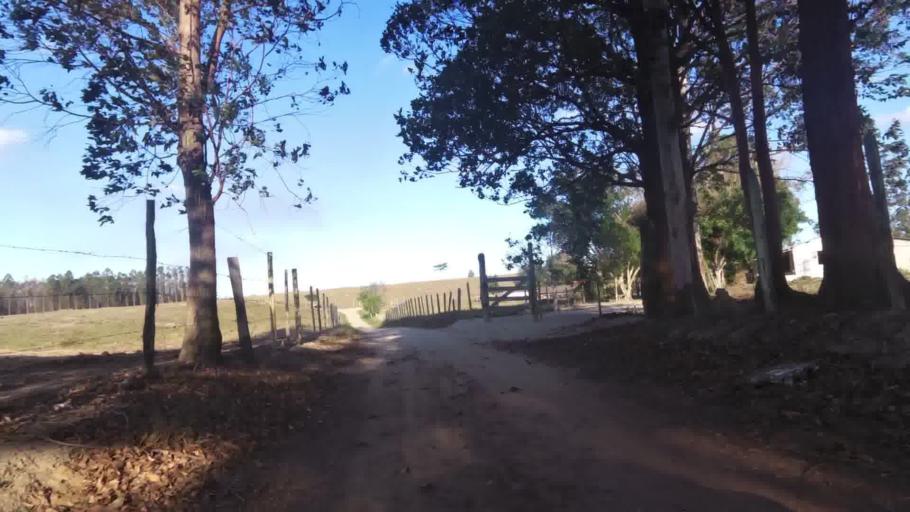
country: BR
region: Espirito Santo
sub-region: Marataizes
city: Marataizes
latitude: -21.1671
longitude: -41.0487
